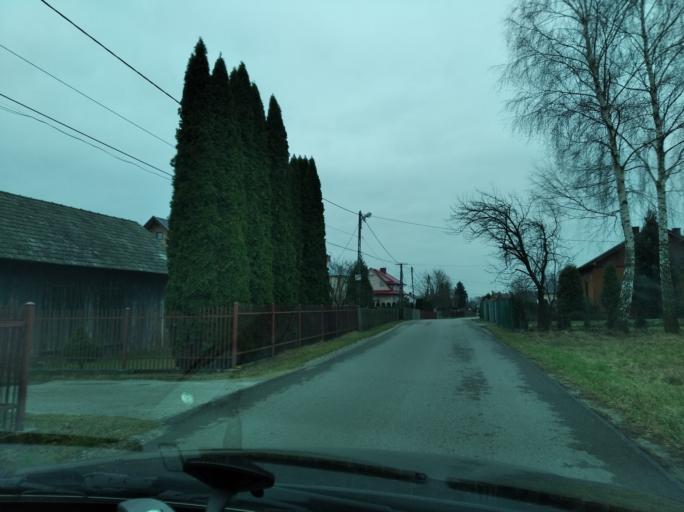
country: PL
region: Subcarpathian Voivodeship
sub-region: Powiat lancucki
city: Rakszawa
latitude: 50.1596
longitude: 22.2310
